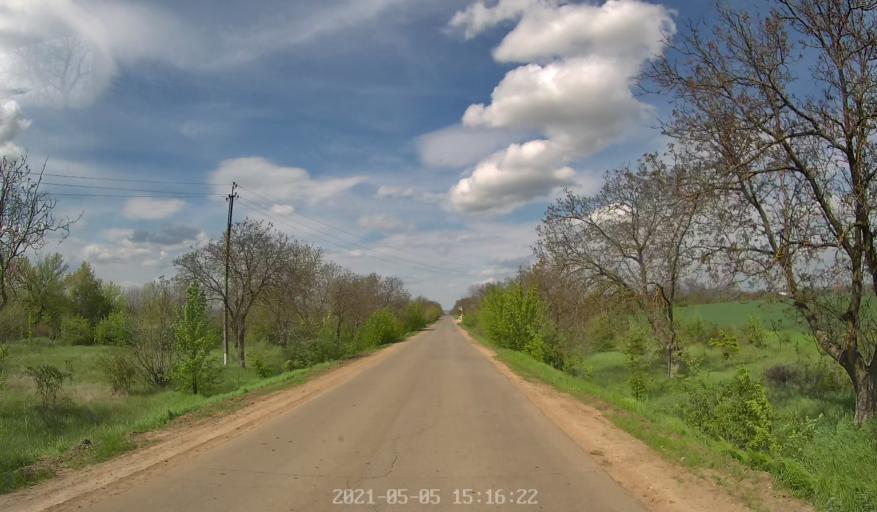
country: MD
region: Criuleni
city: Criuleni
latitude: 47.1020
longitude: 29.1921
